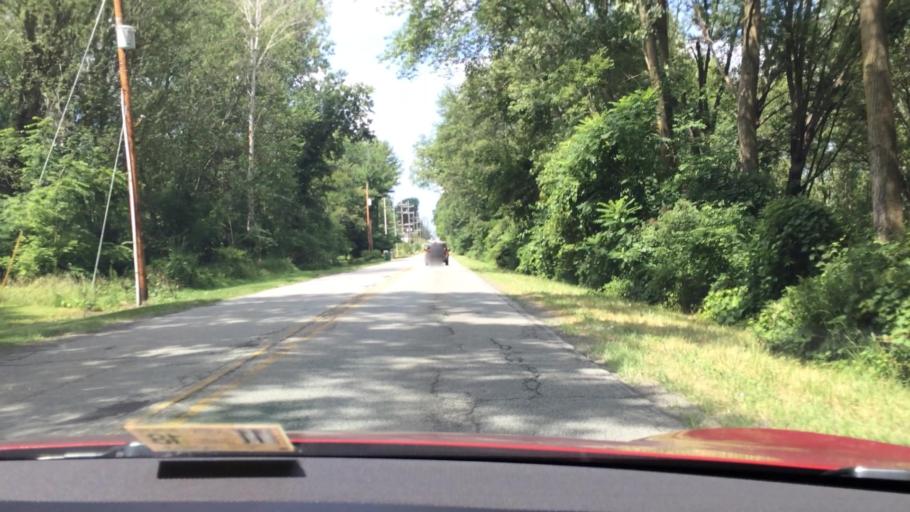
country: US
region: Indiana
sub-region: Saint Joseph County
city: Georgetown
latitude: 41.7091
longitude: -86.2098
